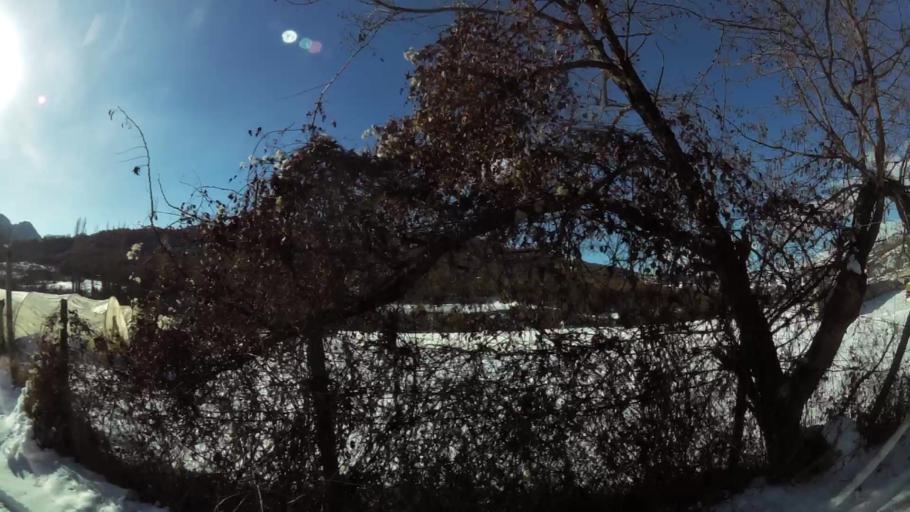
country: MK
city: Ljubin
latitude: 41.9866
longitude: 21.2962
